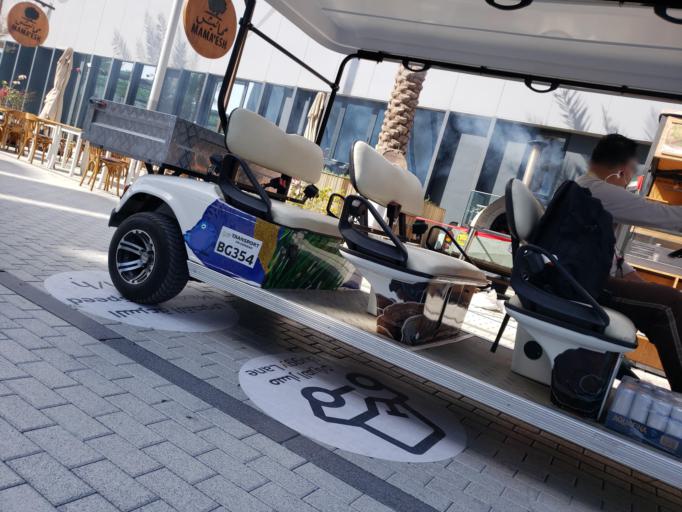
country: AE
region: Dubai
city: Dubai
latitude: 24.9633
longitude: 55.1538
